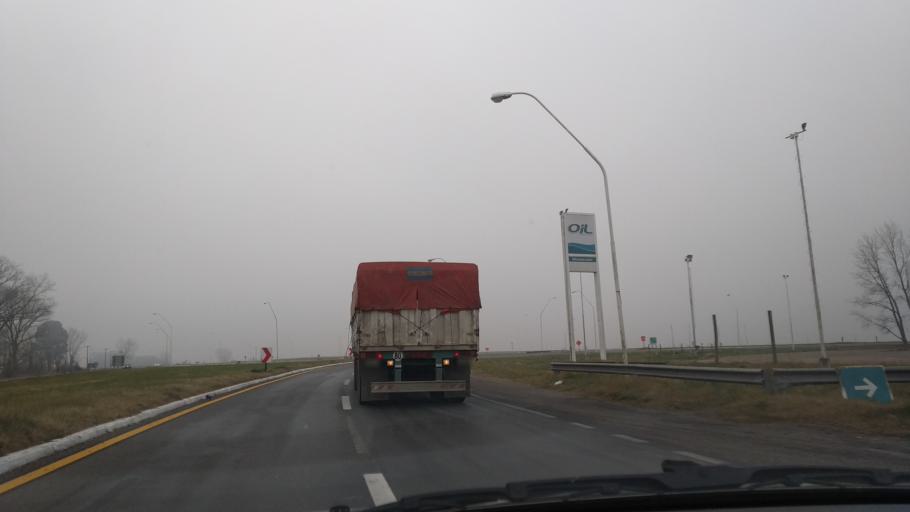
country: AR
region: Buenos Aires
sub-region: Partido de Azul
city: Azul
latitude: -36.8480
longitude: -59.9585
